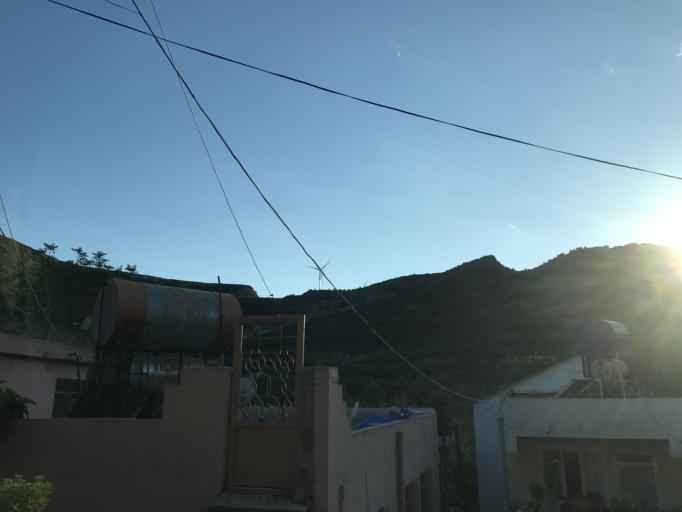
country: TR
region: Hatay
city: Buyukcat
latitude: 36.0761
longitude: 36.0424
